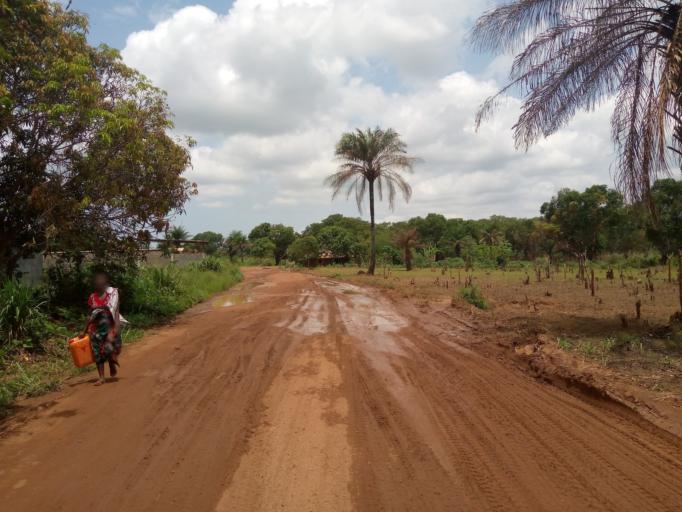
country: SL
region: Western Area
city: Waterloo
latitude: 8.3837
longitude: -12.9568
